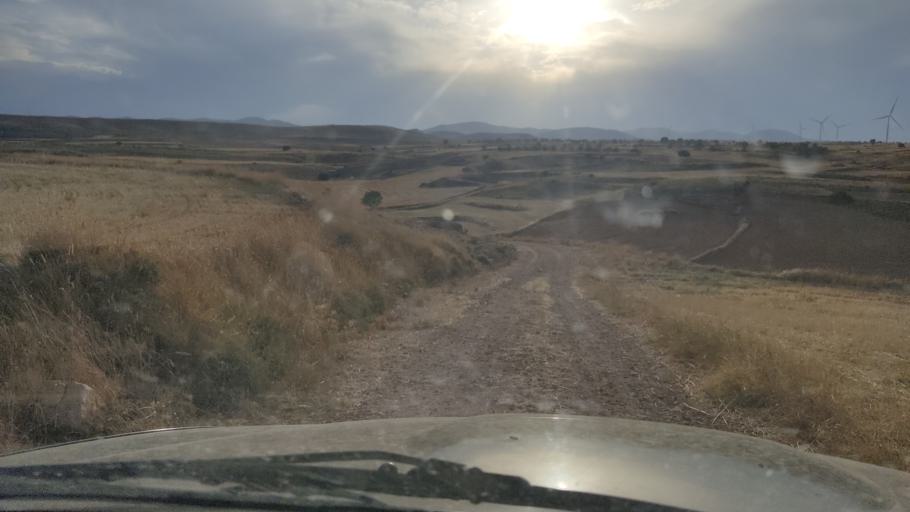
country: ES
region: Aragon
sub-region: Provincia de Zaragoza
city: Plenas
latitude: 41.0673
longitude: -0.9703
